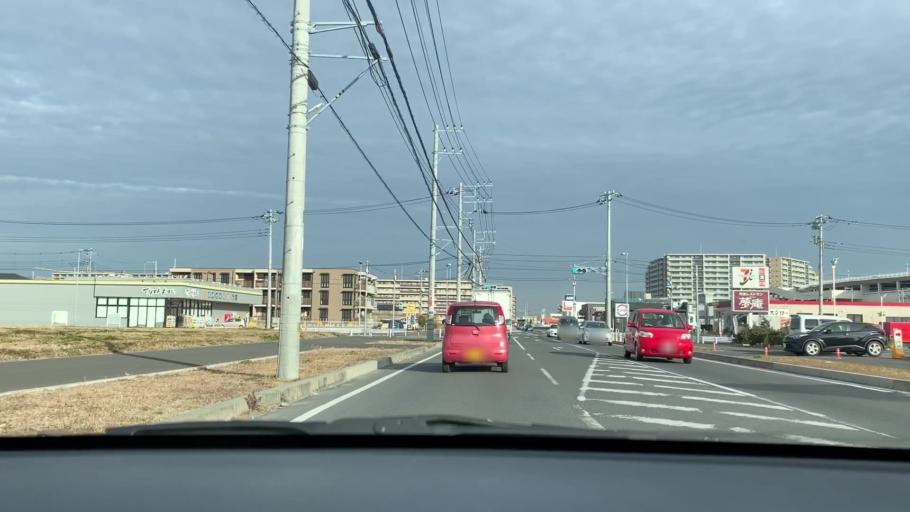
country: JP
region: Chiba
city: Nagareyama
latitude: 35.8306
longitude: 139.8958
